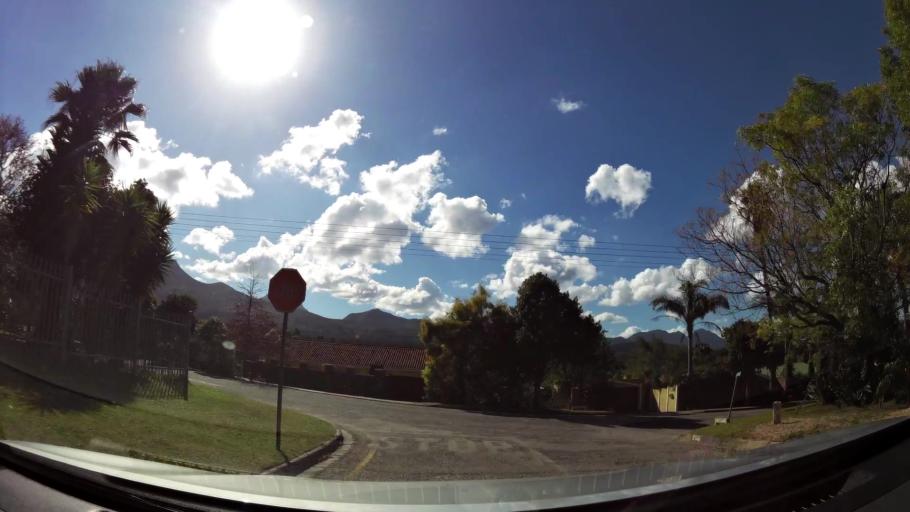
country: ZA
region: Western Cape
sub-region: Eden District Municipality
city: George
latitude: -33.9534
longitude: 22.4815
